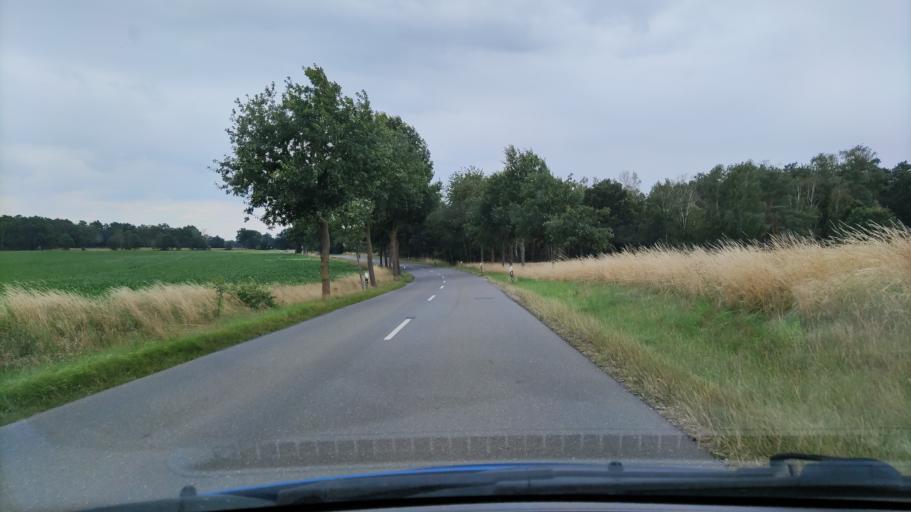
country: DE
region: Lower Saxony
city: Rosche
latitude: 53.0085
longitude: 10.7649
